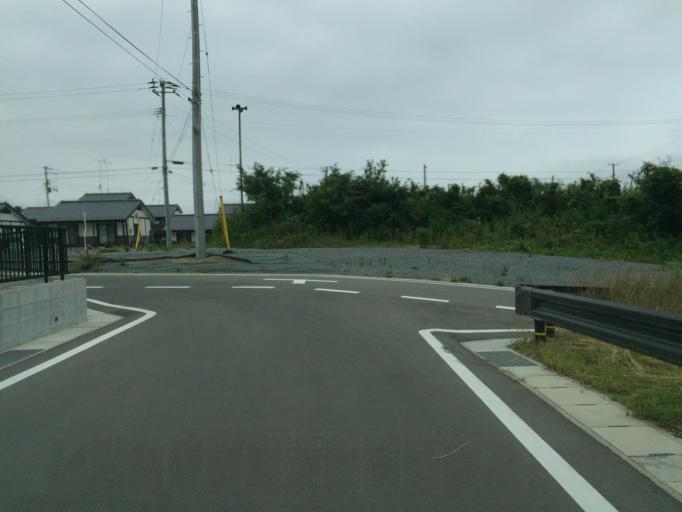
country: JP
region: Miyagi
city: Marumori
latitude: 37.7649
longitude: 140.9745
